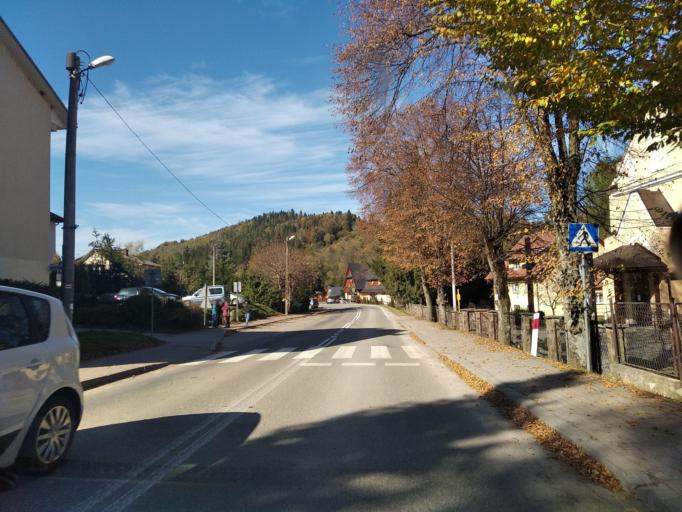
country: PL
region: Subcarpathian Voivodeship
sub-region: Powiat leski
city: Cisna
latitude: 49.2123
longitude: 22.3287
